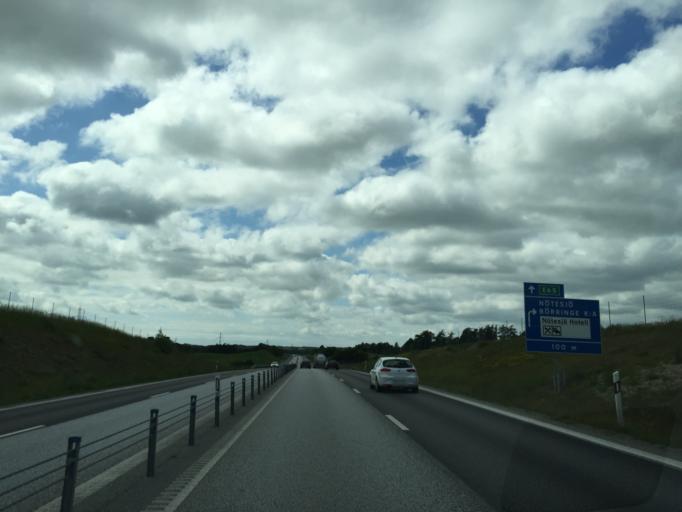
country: SE
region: Skane
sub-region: Trelleborgs Kommun
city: Anderslov
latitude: 55.5031
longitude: 13.3692
